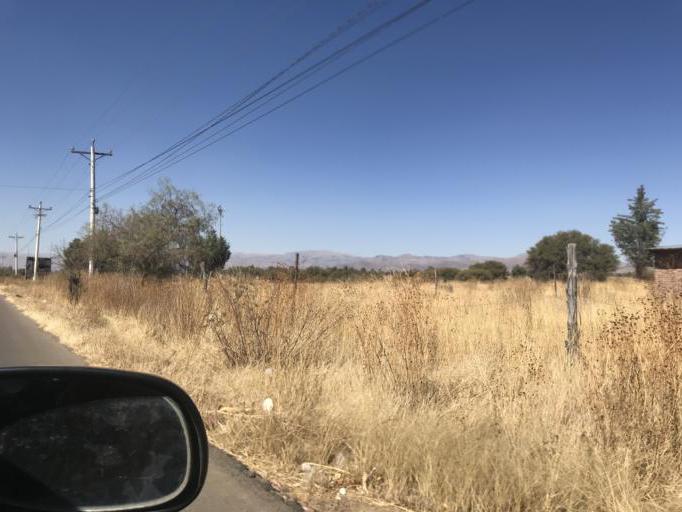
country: BO
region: Cochabamba
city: Cliza
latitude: -17.5996
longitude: -65.9641
